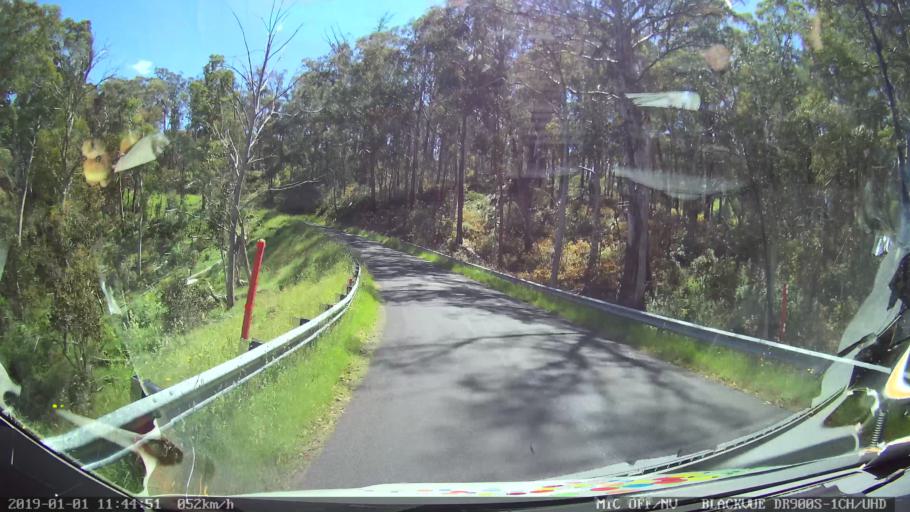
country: AU
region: New South Wales
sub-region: Snowy River
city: Jindabyne
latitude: -35.9010
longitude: 148.3961
